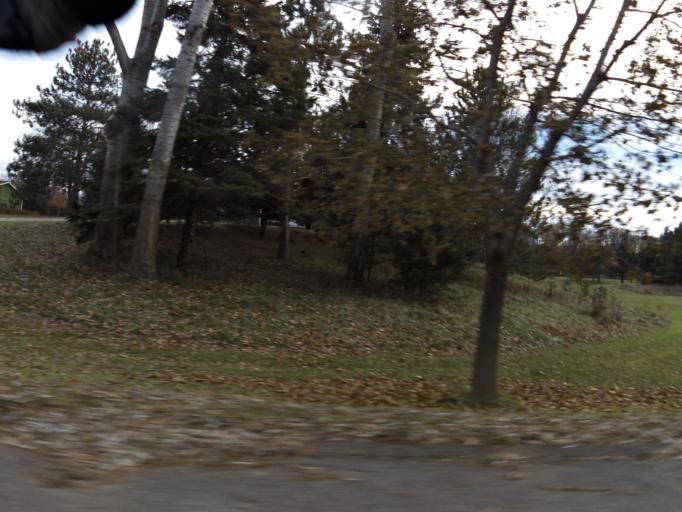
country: US
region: Minnesota
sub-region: Washington County
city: Oak Park Heights
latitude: 45.0122
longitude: -92.8062
